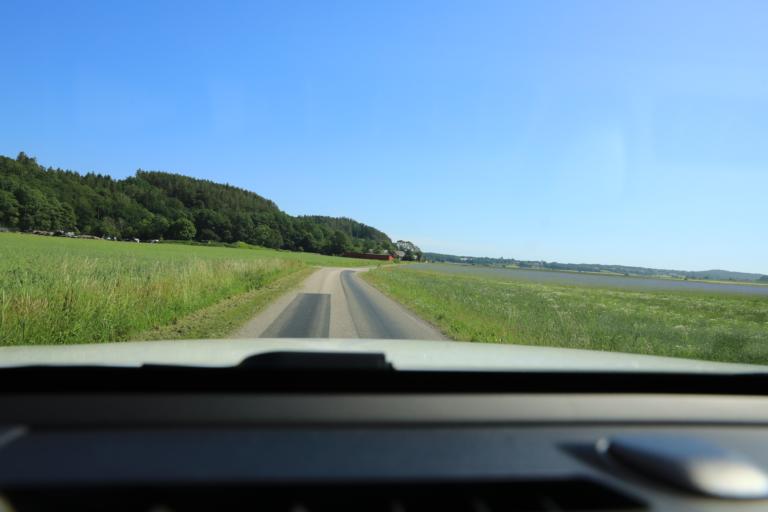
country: SE
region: Halland
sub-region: Varbergs Kommun
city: Veddige
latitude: 57.1835
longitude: 12.3130
